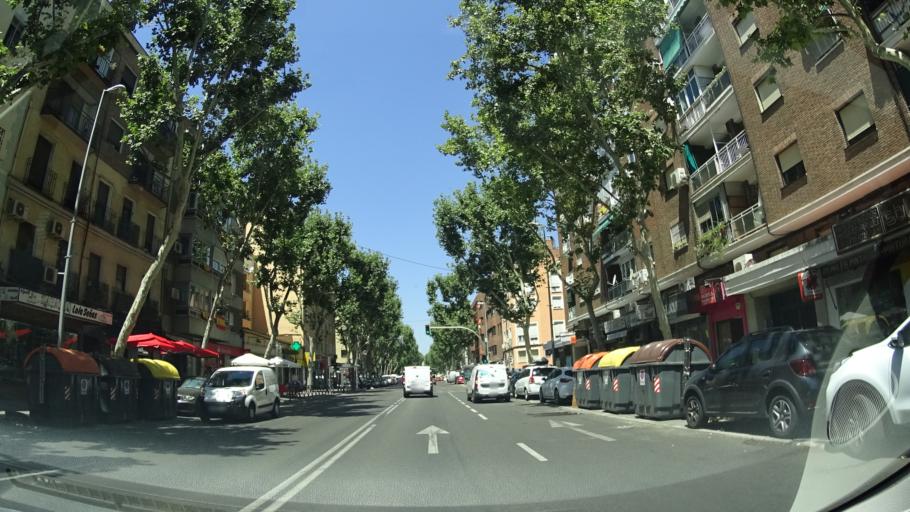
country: ES
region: Madrid
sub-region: Provincia de Madrid
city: Usera
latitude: 40.3954
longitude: -3.7107
